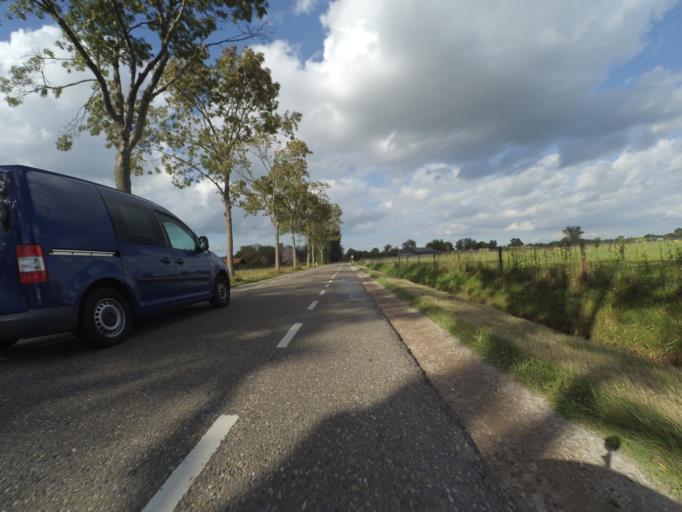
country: NL
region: Gelderland
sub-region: Gemeente Ede
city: Ederveen
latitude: 52.0585
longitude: 5.6066
